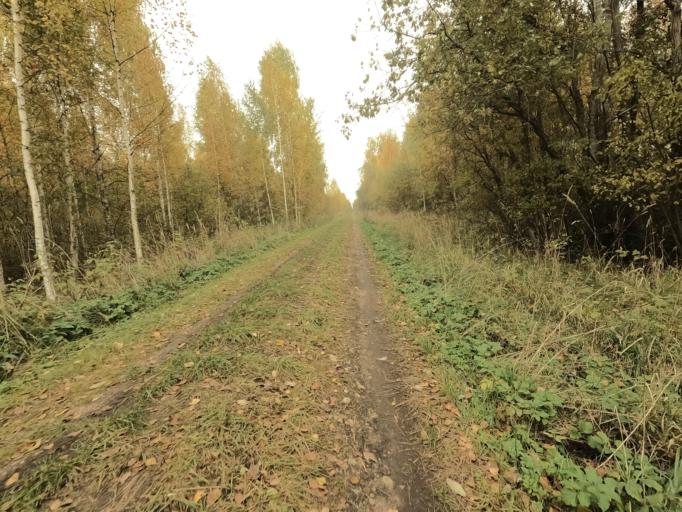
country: RU
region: Novgorod
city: Pankovka
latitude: 58.8833
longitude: 30.9449
